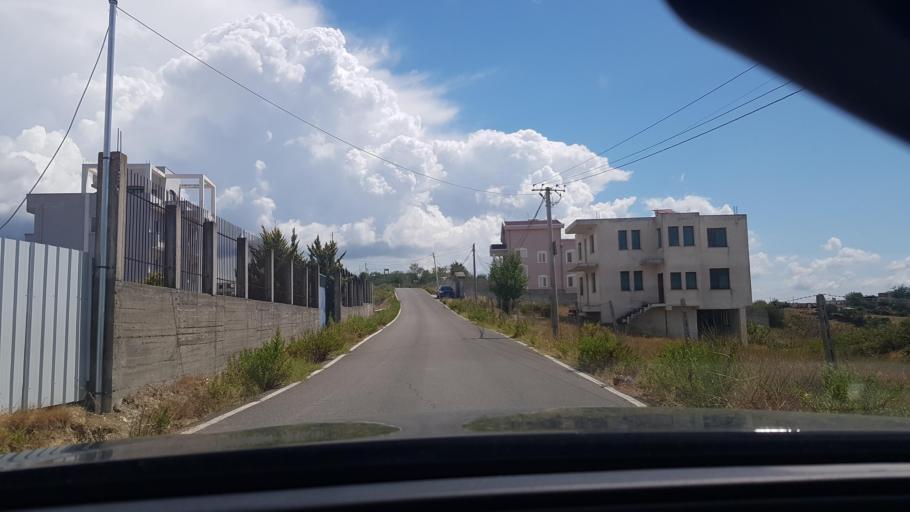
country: AL
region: Durres
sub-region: Rrethi i Durresit
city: Rrashbull
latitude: 41.2934
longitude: 19.5349
